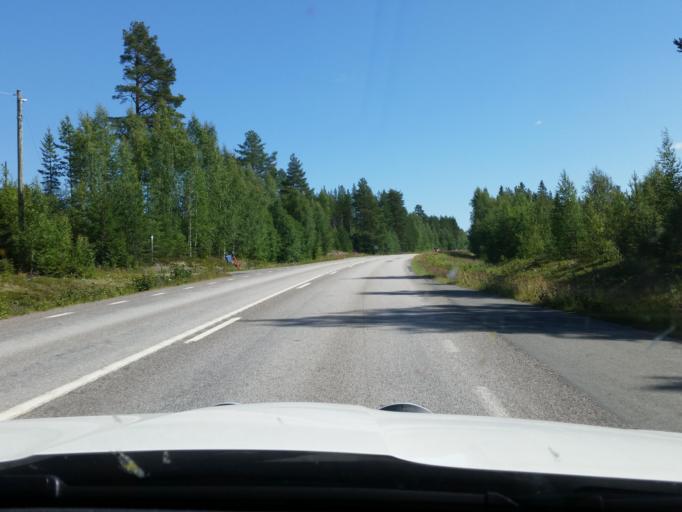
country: SE
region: Norrbotten
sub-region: Alvsbyns Kommun
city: AElvsbyn
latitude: 65.6816
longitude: 20.7955
